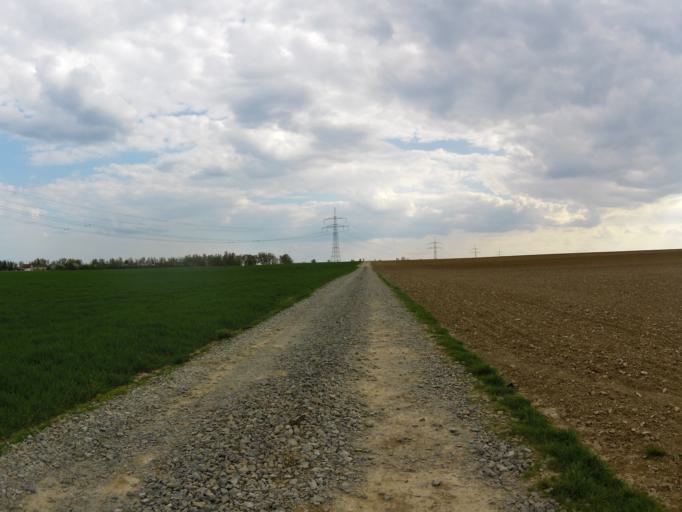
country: DE
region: Bavaria
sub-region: Regierungsbezirk Unterfranken
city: Oberpleichfeld
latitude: 49.8602
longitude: 10.0950
